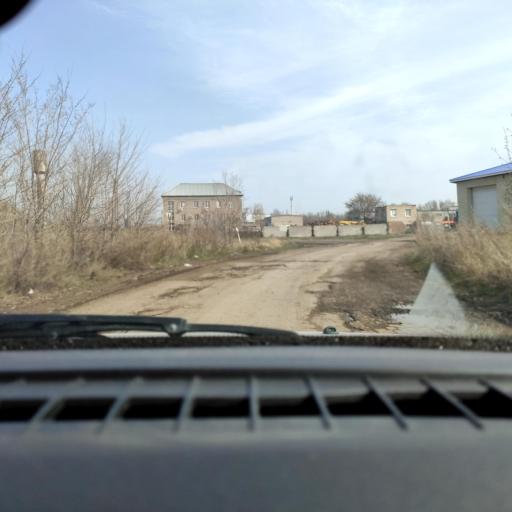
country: RU
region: Samara
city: Dubovyy Umet
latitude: 53.0928
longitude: 50.3056
